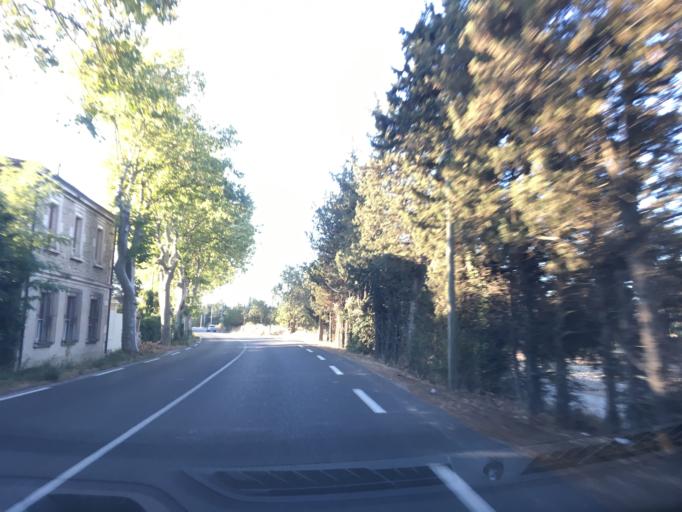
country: FR
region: Provence-Alpes-Cote d'Azur
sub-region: Departement des Bouches-du-Rhone
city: Senas
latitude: 43.7326
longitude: 5.0806
